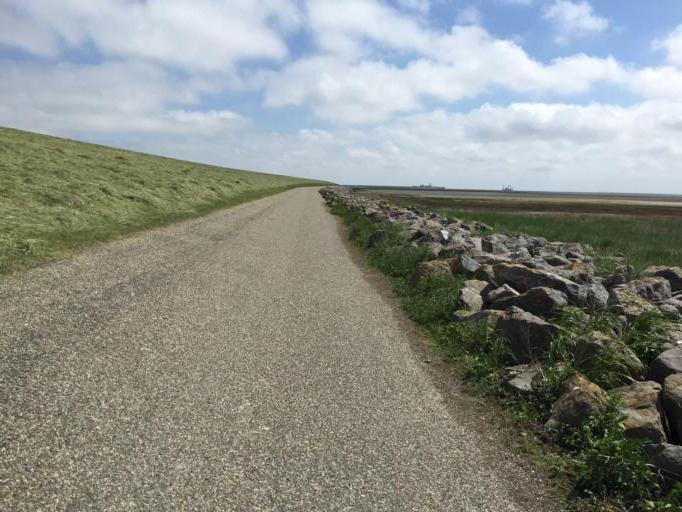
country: NL
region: Friesland
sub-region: Gemeente Schiermonnikoog
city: Schiermonnikoog
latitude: 53.4726
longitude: 6.1686
